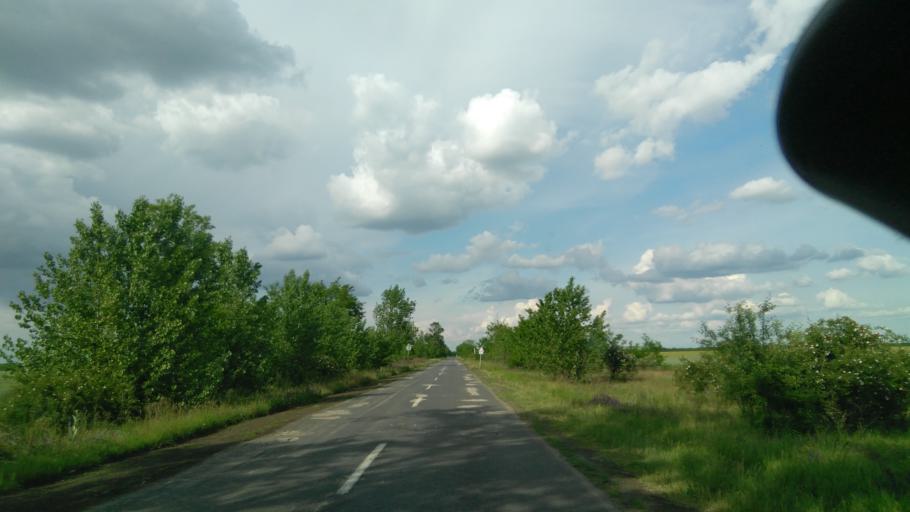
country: HU
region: Bekes
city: Battonya
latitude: 46.3087
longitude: 21.0655
